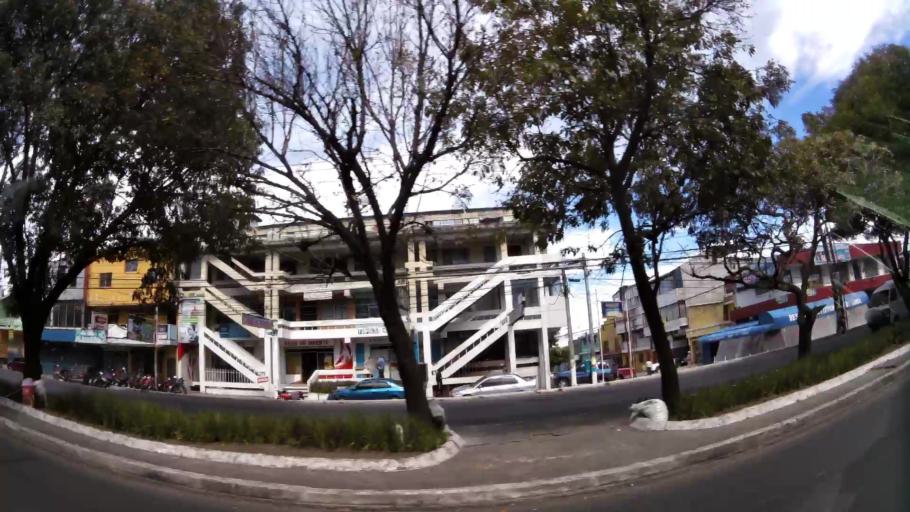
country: GT
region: Guatemala
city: Mixco
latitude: 14.6429
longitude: -90.5723
